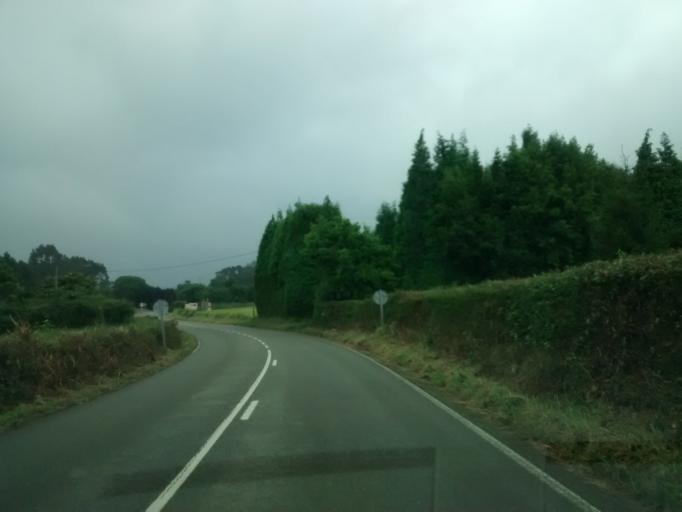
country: ES
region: Asturias
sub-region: Province of Asturias
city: Villaviciosa
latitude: 43.5261
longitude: -5.3737
